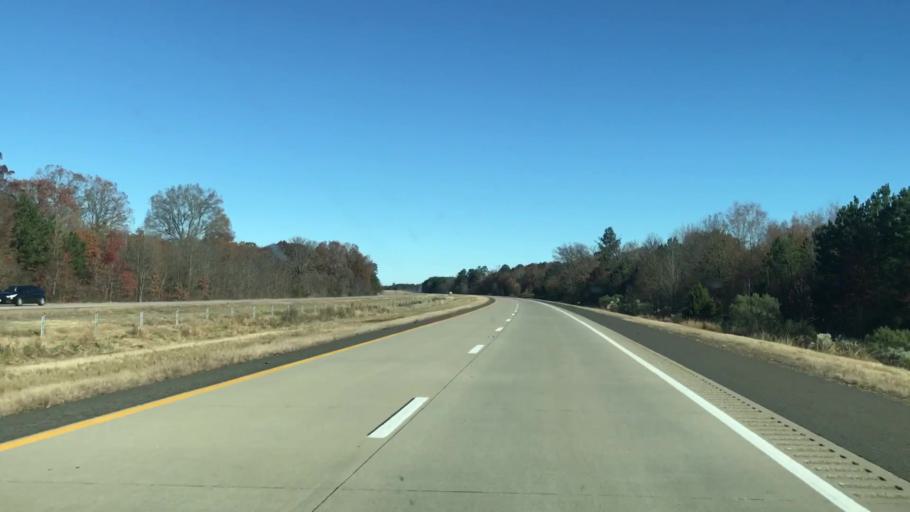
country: US
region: Texas
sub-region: Bowie County
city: Texarkana
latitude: 33.2106
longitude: -93.8742
